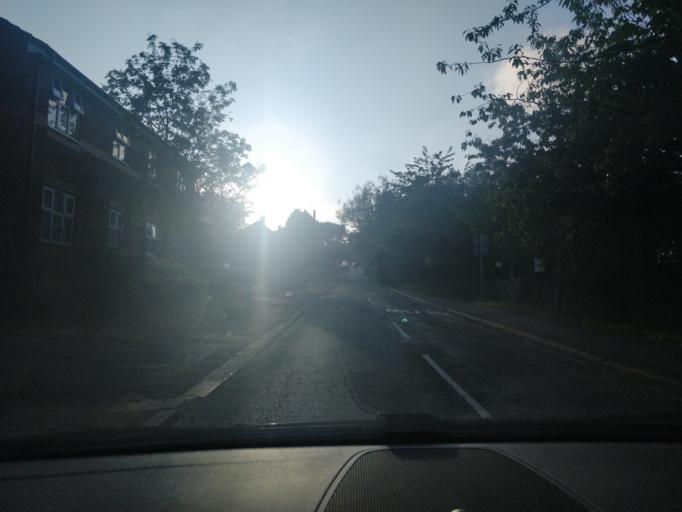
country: GB
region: England
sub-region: Lancashire
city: Appley Bridge
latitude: 53.5436
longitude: -2.7303
